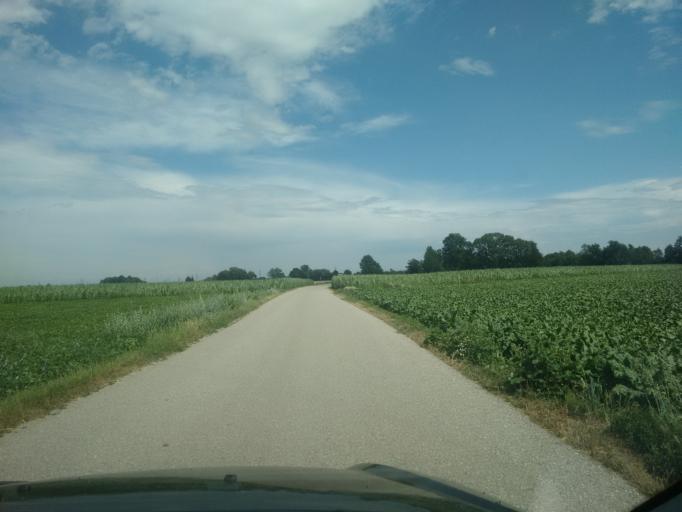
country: AT
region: Upper Austria
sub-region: Wels-Land
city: Gunskirchen
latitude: 48.1656
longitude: 13.9637
